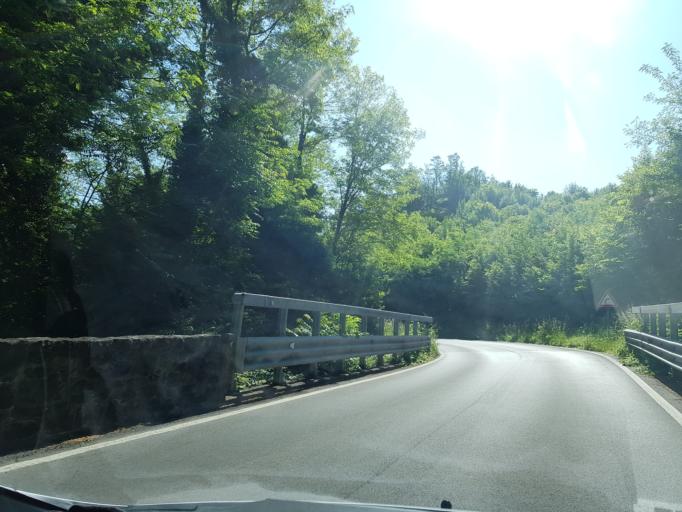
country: IT
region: Tuscany
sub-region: Provincia di Lucca
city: Camporgiano
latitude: 44.1683
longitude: 10.3268
